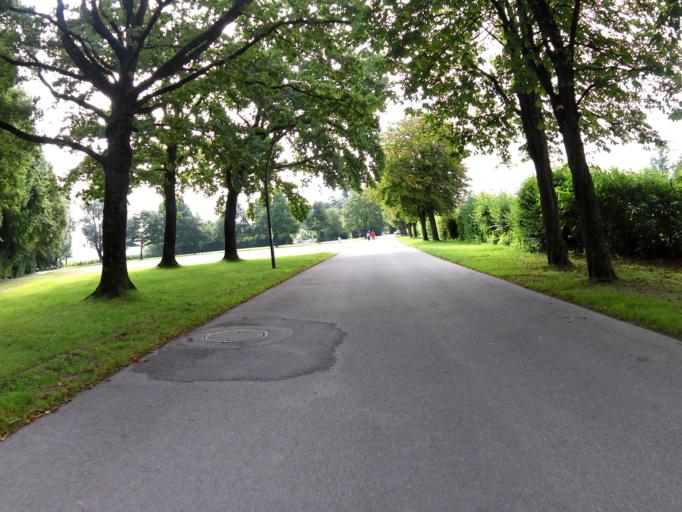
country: DE
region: Bavaria
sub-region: Upper Bavaria
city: Diessen am Ammersee
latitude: 47.9529
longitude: 11.1061
